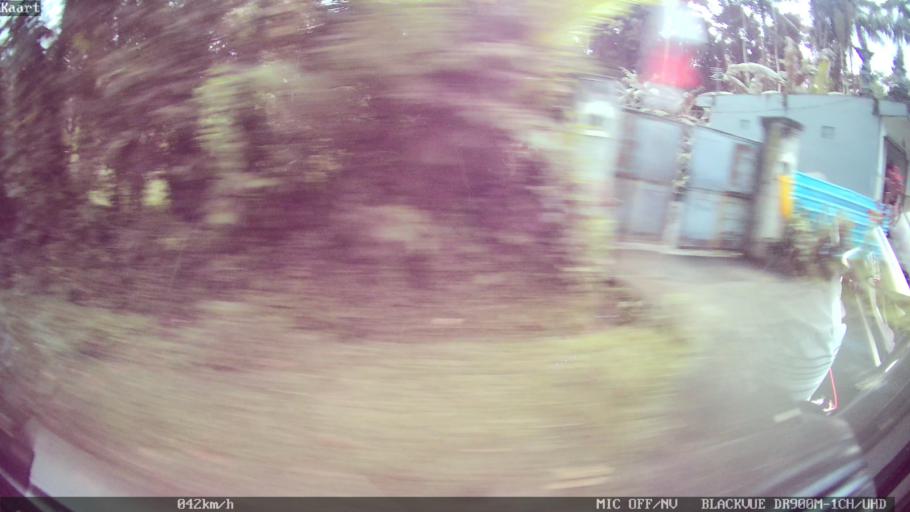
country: ID
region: Bali
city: Pegongan
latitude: -8.4736
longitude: 115.2325
